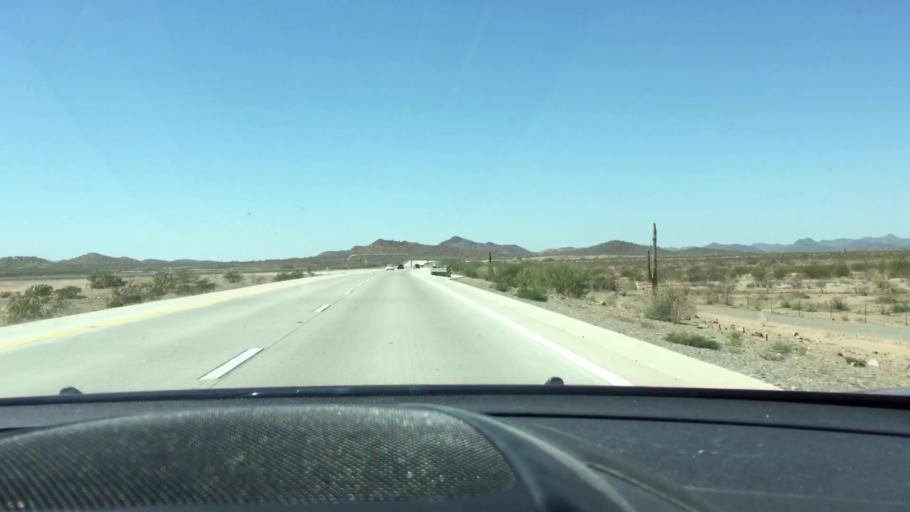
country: US
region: Arizona
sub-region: Maricopa County
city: Anthem
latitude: 33.7698
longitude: -112.1550
